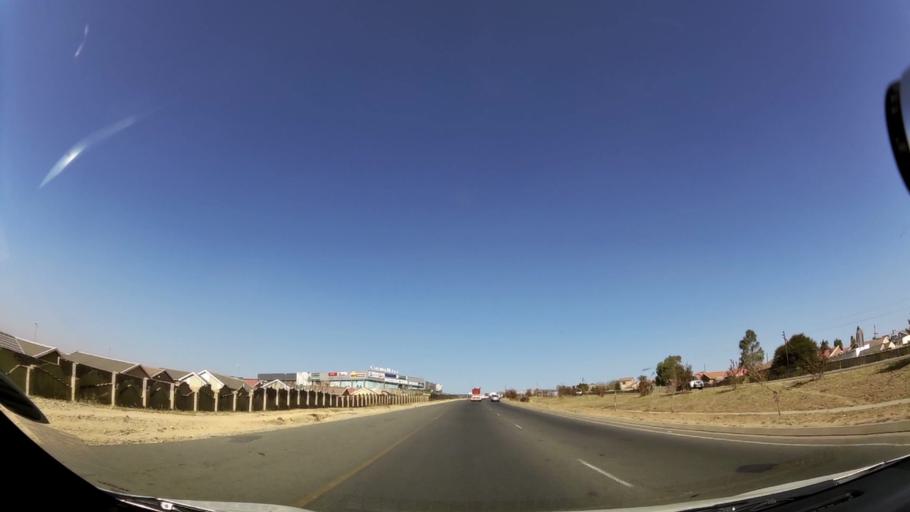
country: ZA
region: Gauteng
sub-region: West Rand District Municipality
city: Muldersdriseloop
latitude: -26.0113
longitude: 27.9371
